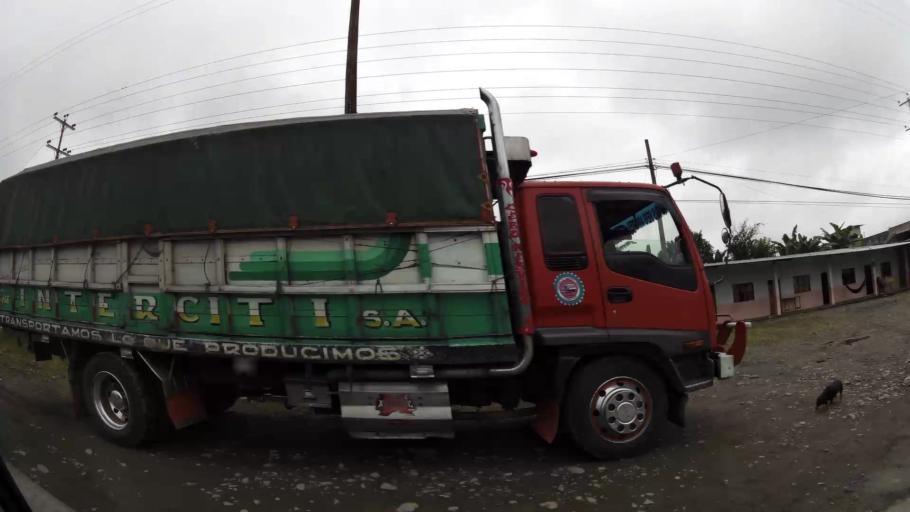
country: EC
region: Santo Domingo de los Tsachilas
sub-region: Canton Santo Domingo de los Colorados
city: Santo Domingo de los Colorados
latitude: -0.2557
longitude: -79.1282
